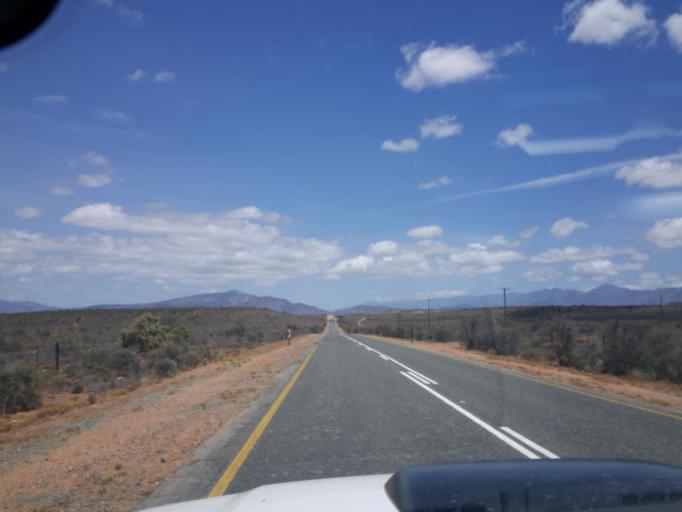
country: ZA
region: Western Cape
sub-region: Central Karoo District Municipality
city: Prince Albert
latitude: -33.5407
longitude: 21.7991
